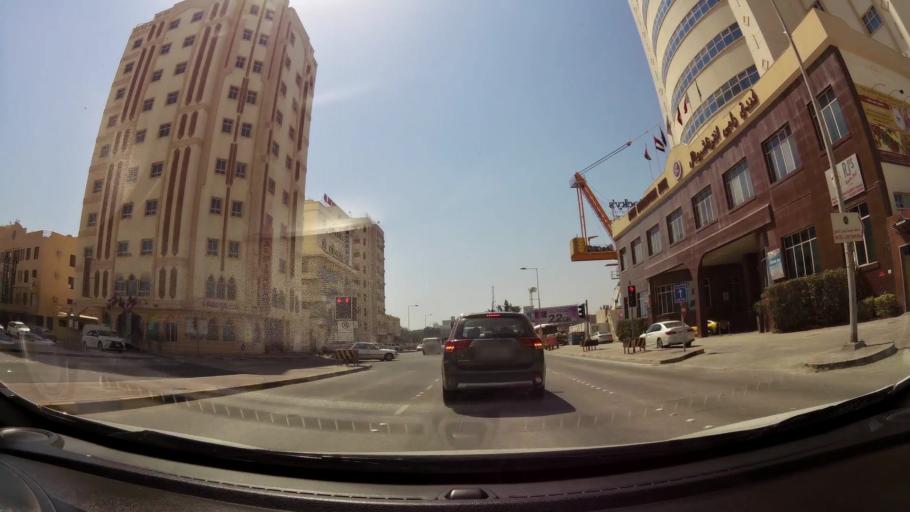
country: BH
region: Manama
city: Manama
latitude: 26.2123
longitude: 50.6098
